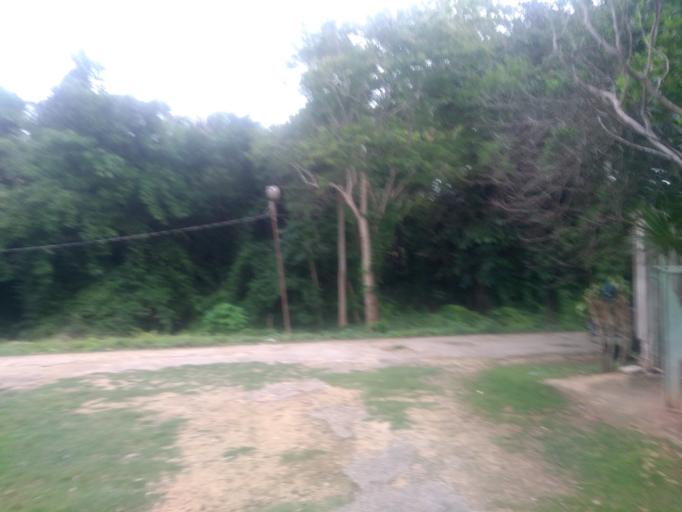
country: PH
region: Central Visayas
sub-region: Province of Siquijor
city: Lazi
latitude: 9.1299
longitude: 123.6327
